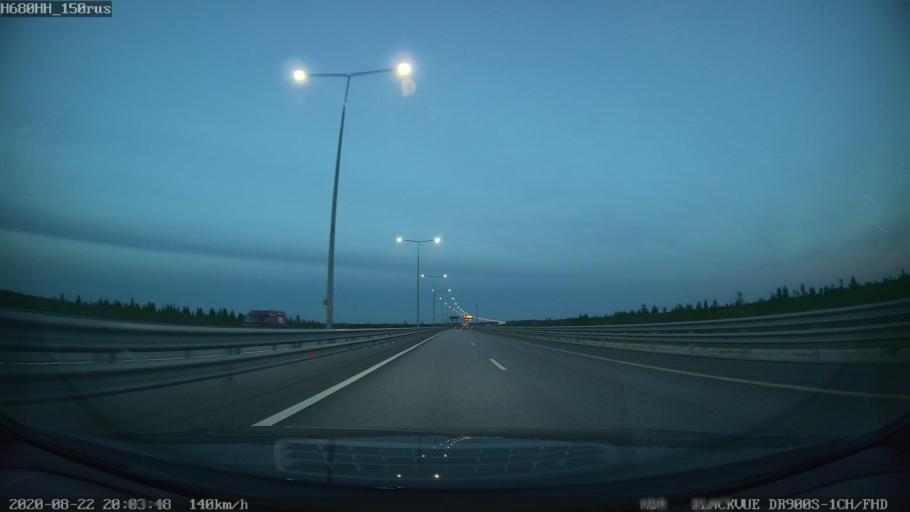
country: RU
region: Tverskaya
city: Radchenko
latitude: 56.6535
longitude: 36.3756
